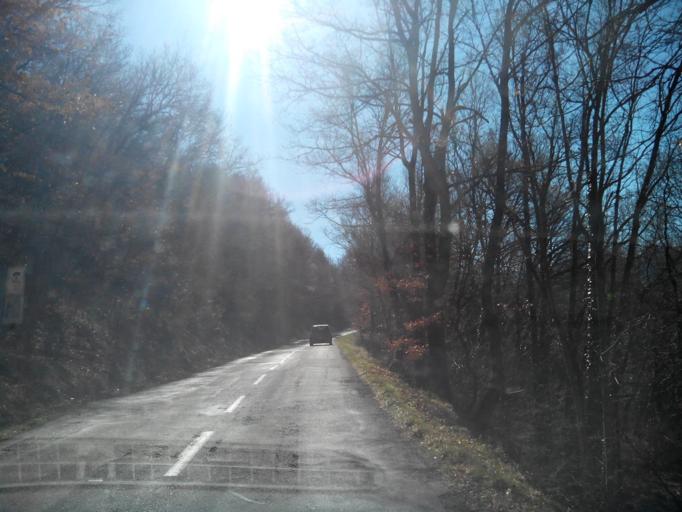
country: ES
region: Catalonia
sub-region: Provincia de Lleida
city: Lles de Cerdanya
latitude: 42.3786
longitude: 1.6788
